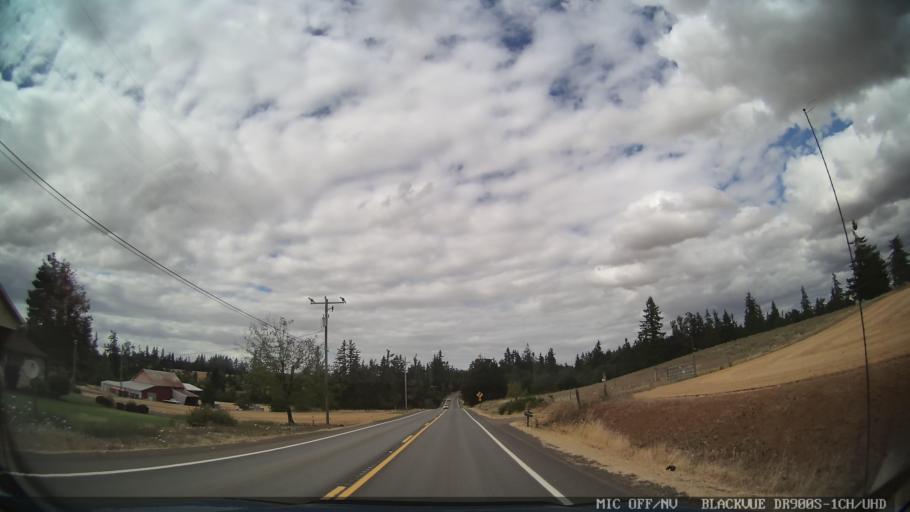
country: US
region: Oregon
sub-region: Marion County
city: Sublimity
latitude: 44.8457
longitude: -122.7945
